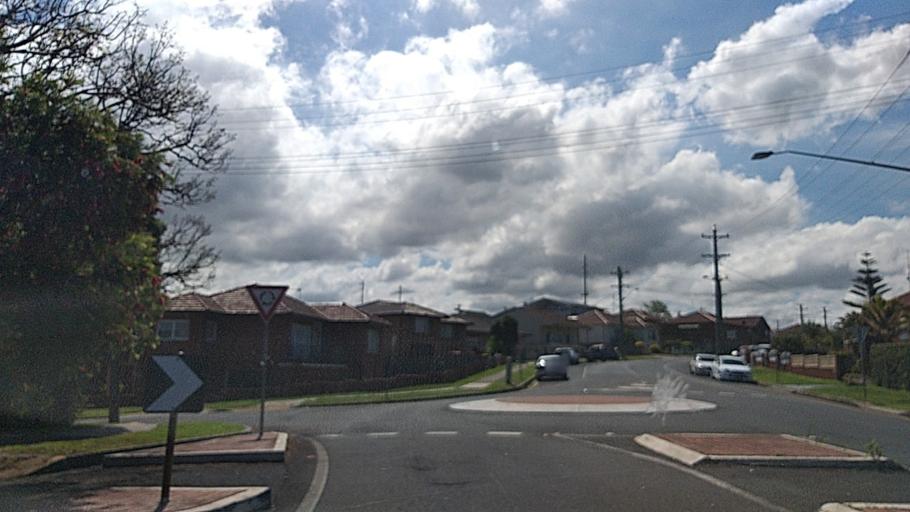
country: AU
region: New South Wales
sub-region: Wollongong
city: Lake Heights
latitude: -34.4808
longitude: 150.8723
